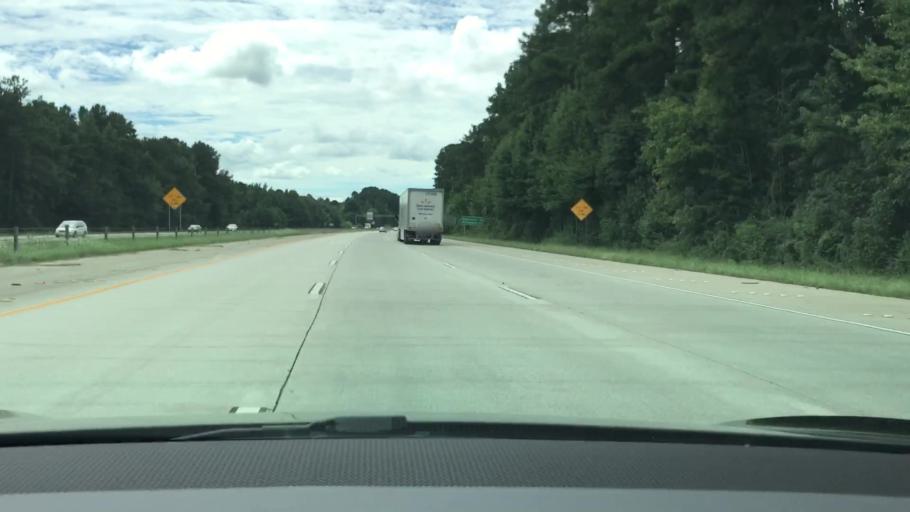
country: US
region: Georgia
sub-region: Coweta County
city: Grantville
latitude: 33.2272
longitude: -84.8110
